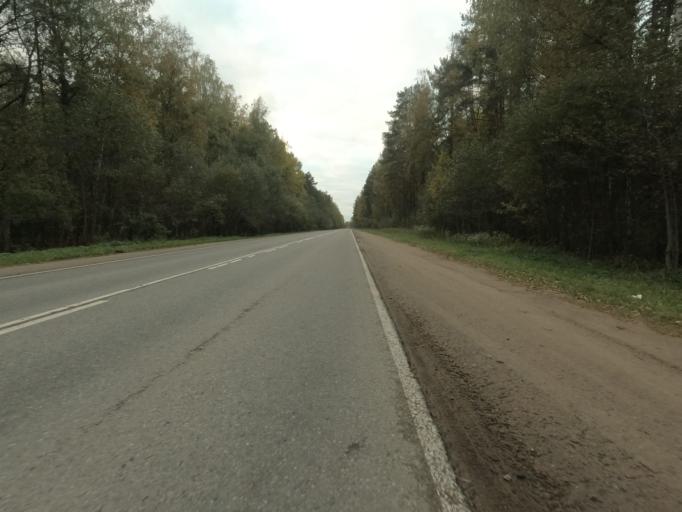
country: RU
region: Leningrad
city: Pavlovo
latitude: 59.8063
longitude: 30.9331
